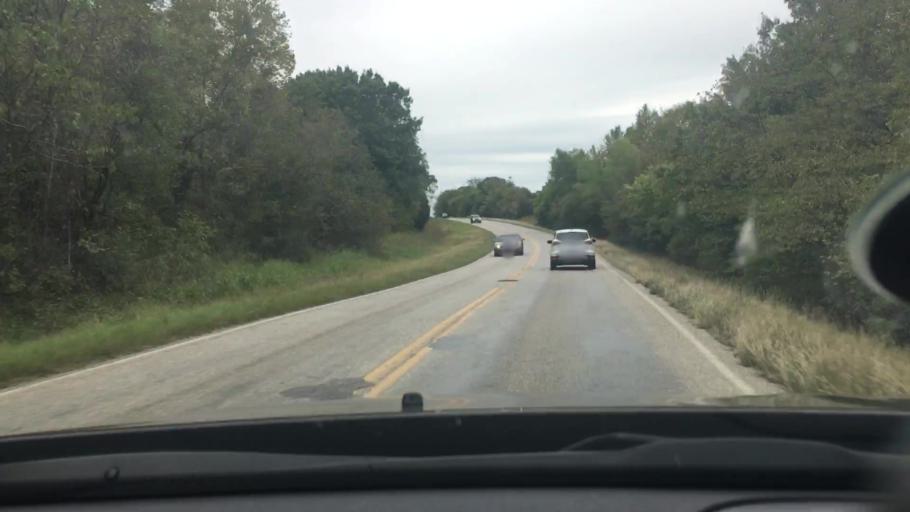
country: US
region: Oklahoma
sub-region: Johnston County
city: Tishomingo
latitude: 34.3329
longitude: -96.4195
